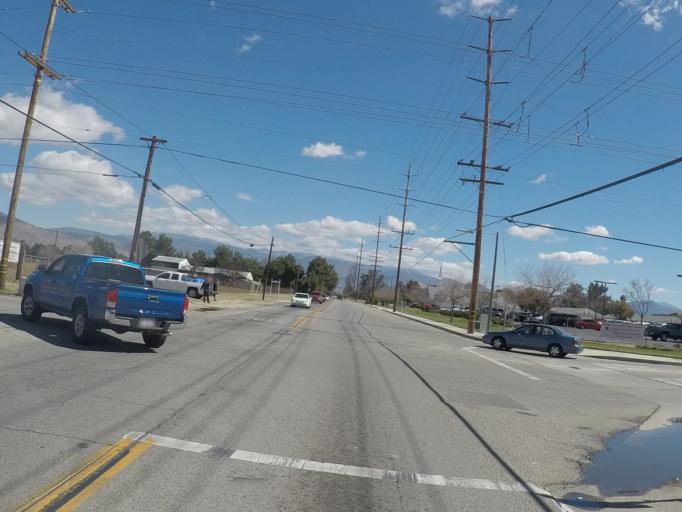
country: US
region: California
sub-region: Riverside County
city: Hemet
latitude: 33.7728
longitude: -116.9982
